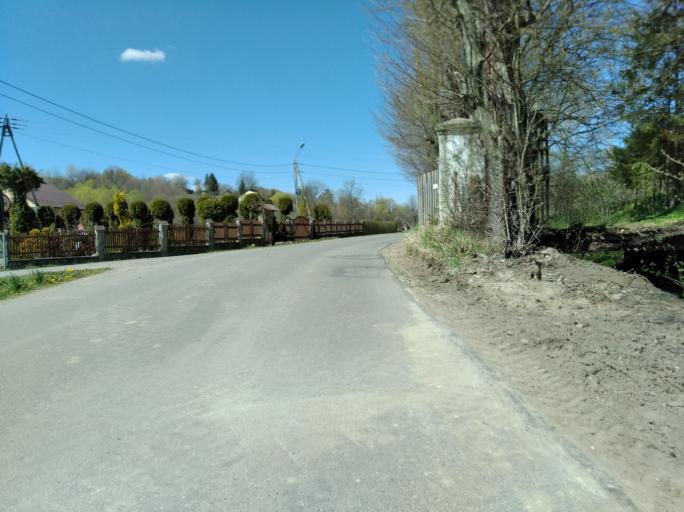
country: PL
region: Subcarpathian Voivodeship
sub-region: Powiat brzozowski
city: Jablonka
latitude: 49.7080
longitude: 22.1449
